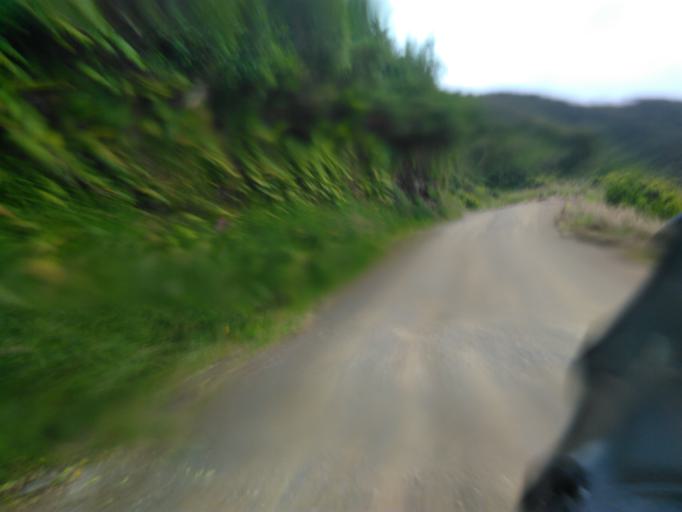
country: NZ
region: Bay of Plenty
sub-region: Opotiki District
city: Opotiki
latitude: -38.0935
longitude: 177.4857
